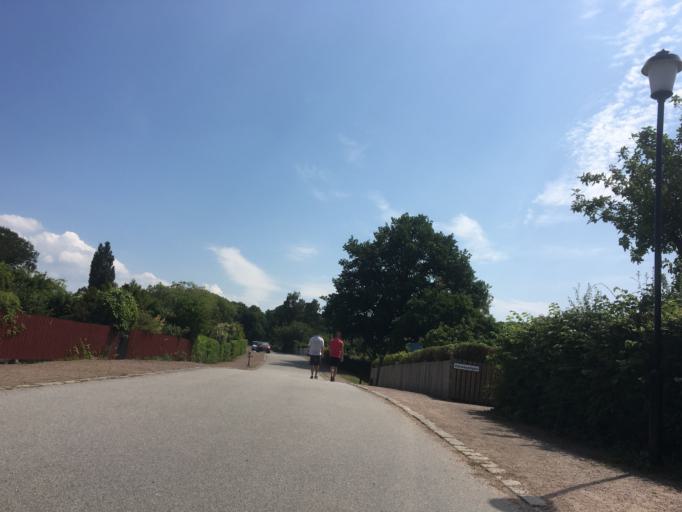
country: SE
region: Skane
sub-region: Landskrona
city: Landskrona
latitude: 55.8751
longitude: 12.8263
